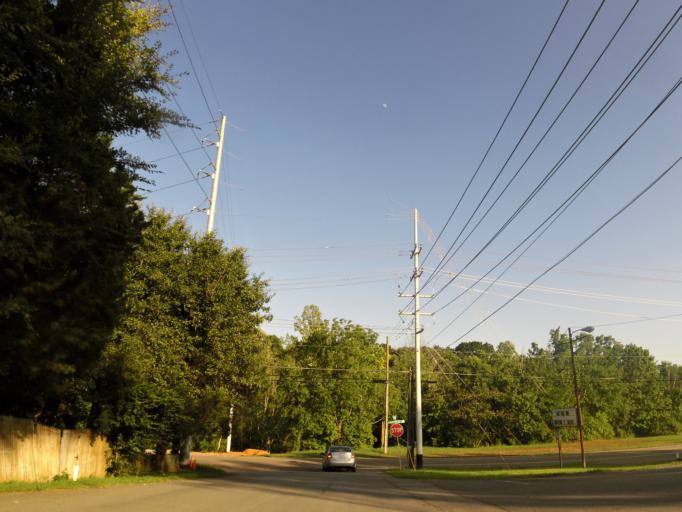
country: US
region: Tennessee
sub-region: Knox County
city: Knoxville
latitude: 35.9153
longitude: -83.9354
